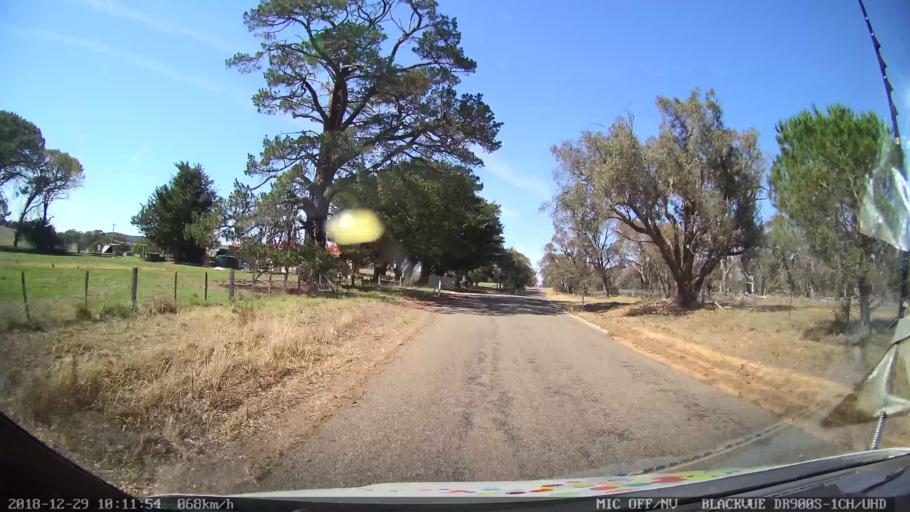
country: AU
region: New South Wales
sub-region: Yass Valley
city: Gundaroo
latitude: -34.8885
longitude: 149.4508
